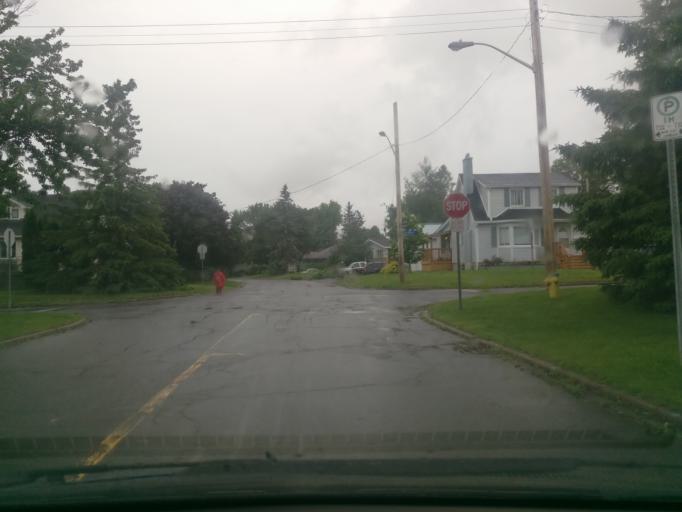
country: CA
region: Ontario
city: Ottawa
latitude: 45.4337
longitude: -75.6454
